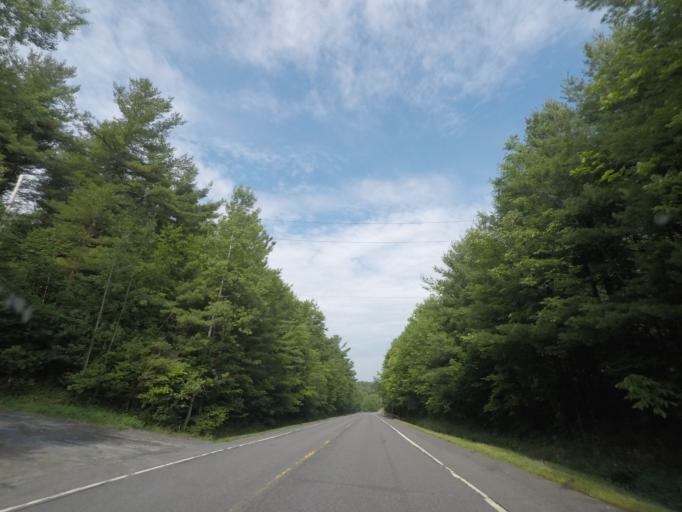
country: US
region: New York
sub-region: Rensselaer County
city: Averill Park
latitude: 42.6513
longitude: -73.5605
